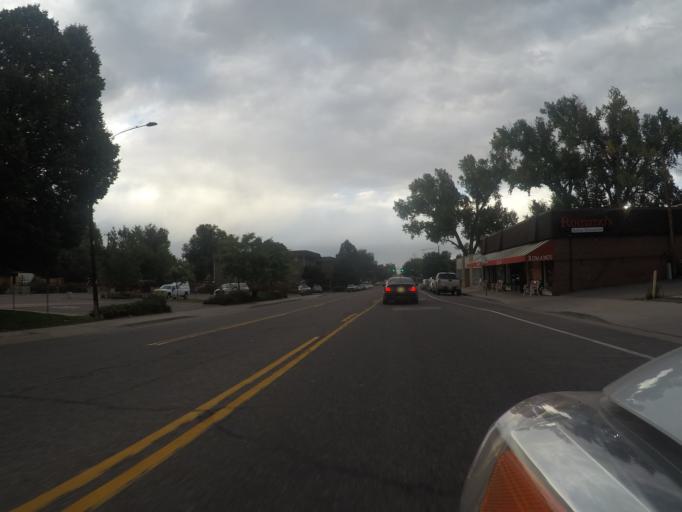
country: US
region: Colorado
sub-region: Arapahoe County
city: Littleton
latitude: 39.6137
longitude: -105.0069
